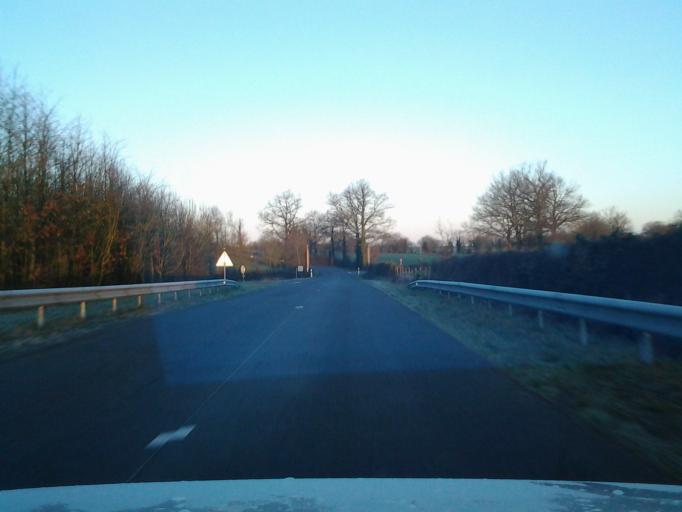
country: FR
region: Pays de la Loire
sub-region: Departement de la Vendee
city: La Gaubretiere
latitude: 46.9254
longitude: -1.0255
